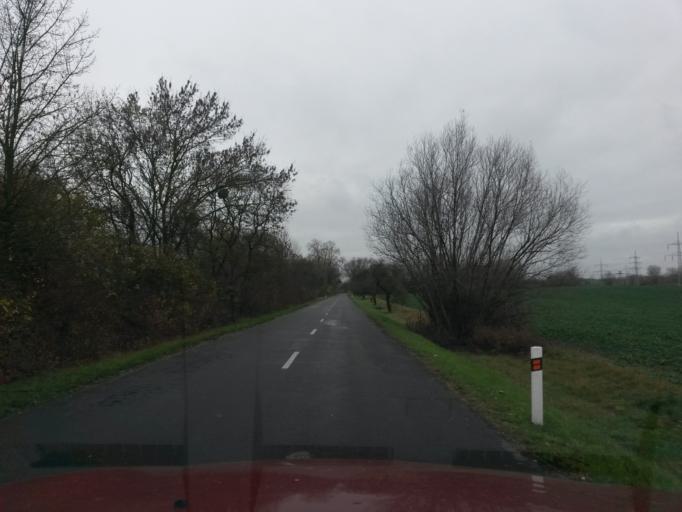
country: SK
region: Kosicky
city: Cierna nad Tisou
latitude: 48.5533
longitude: 21.9671
